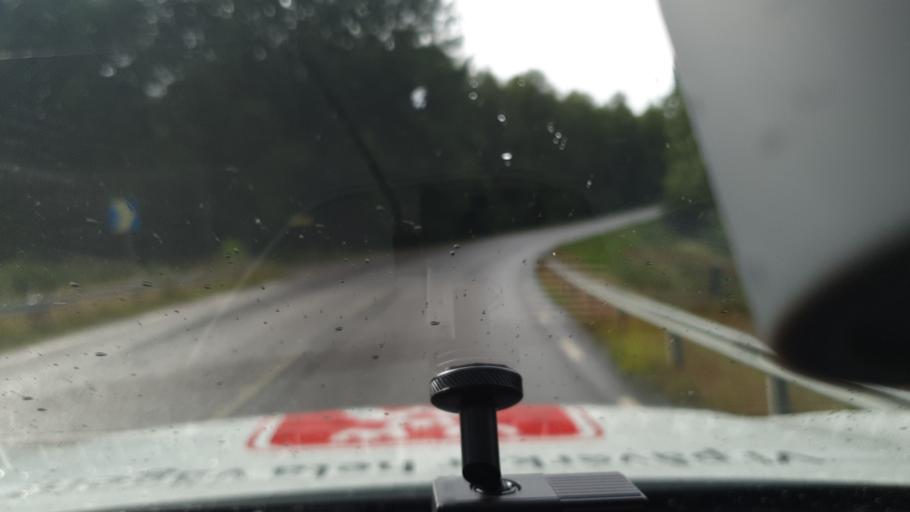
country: SE
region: Vaermland
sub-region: Sunne Kommun
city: Sunne
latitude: 59.7985
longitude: 13.0562
